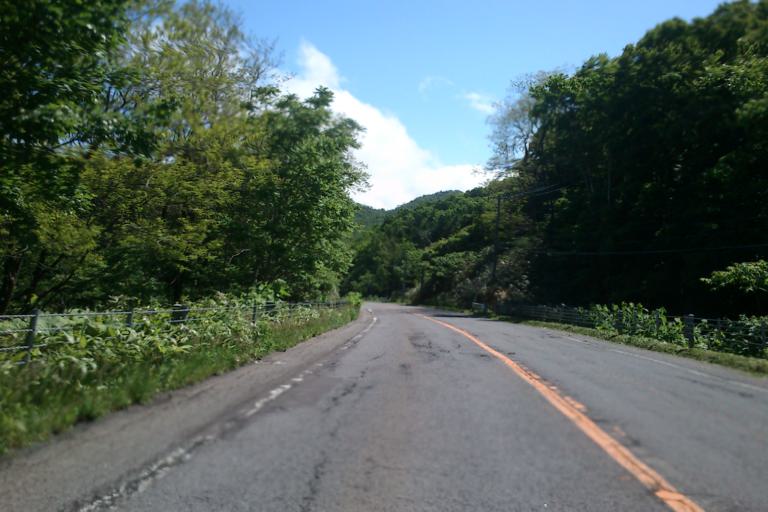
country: JP
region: Hokkaido
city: Ishikari
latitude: 43.5545
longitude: 141.3978
